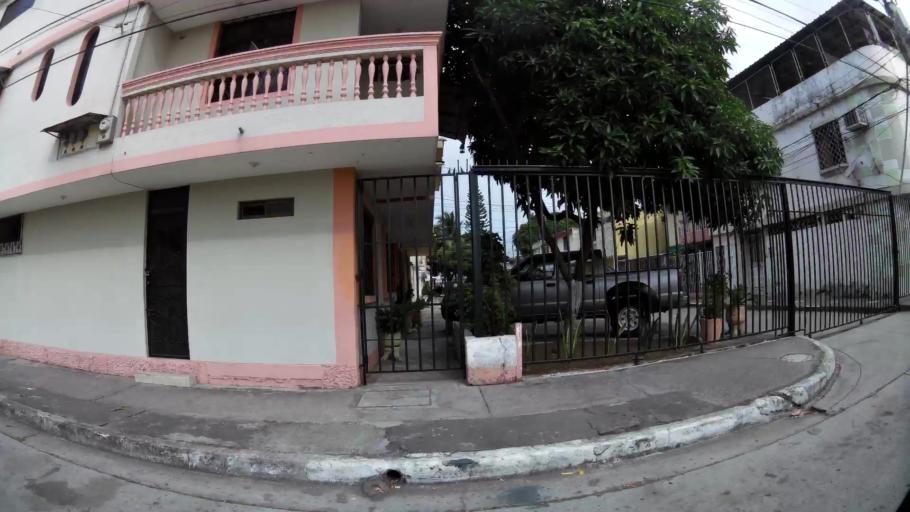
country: EC
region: Guayas
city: Eloy Alfaro
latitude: -2.1376
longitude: -79.8859
